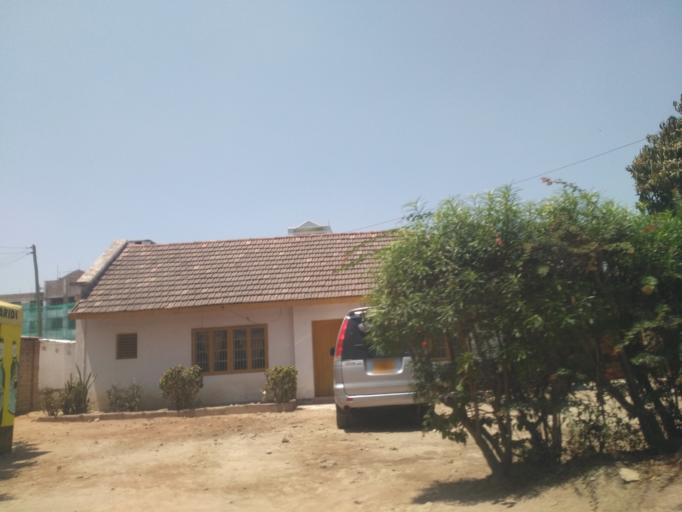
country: TZ
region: Dodoma
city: Dodoma
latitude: -6.1752
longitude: 35.7481
